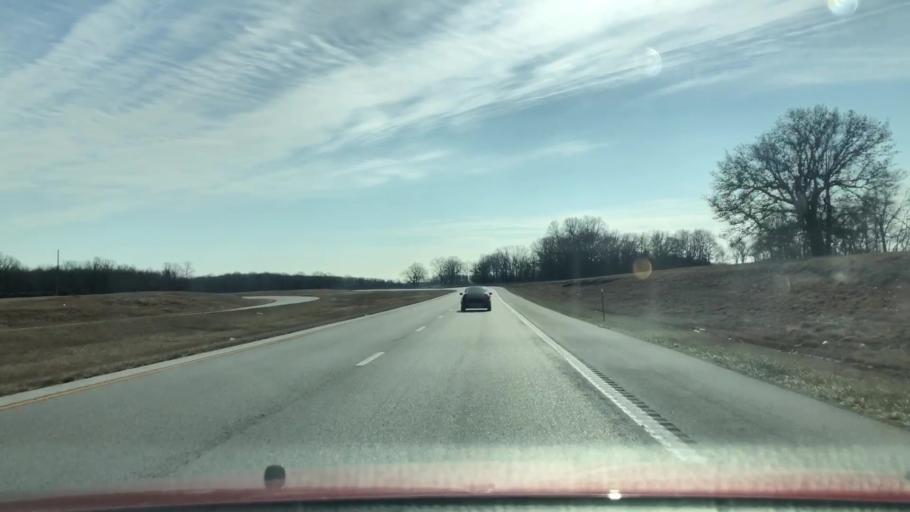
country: US
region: Missouri
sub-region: Webster County
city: Seymour
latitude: 37.1345
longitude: -92.7433
